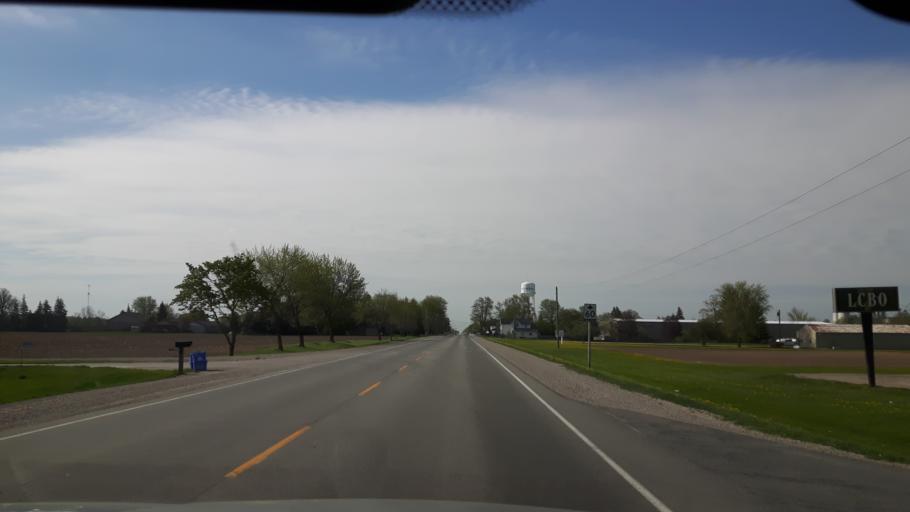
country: CA
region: Ontario
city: Bluewater
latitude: 43.4410
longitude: -81.5000
